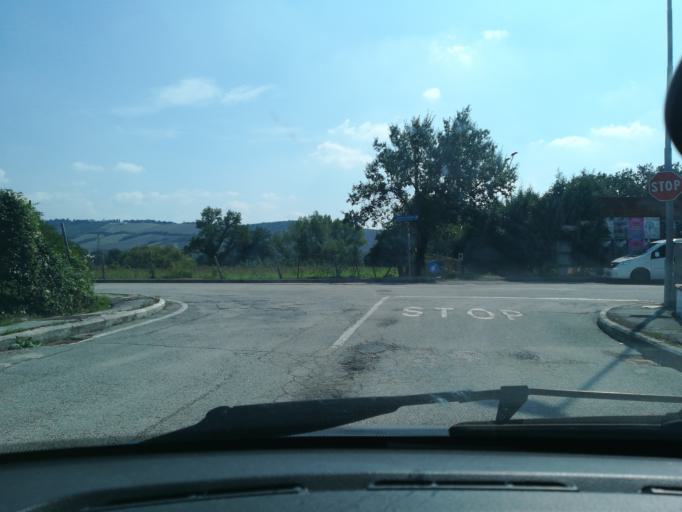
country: IT
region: The Marches
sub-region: Provincia di Macerata
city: Casette Verdini
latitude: 43.2500
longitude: 13.4062
